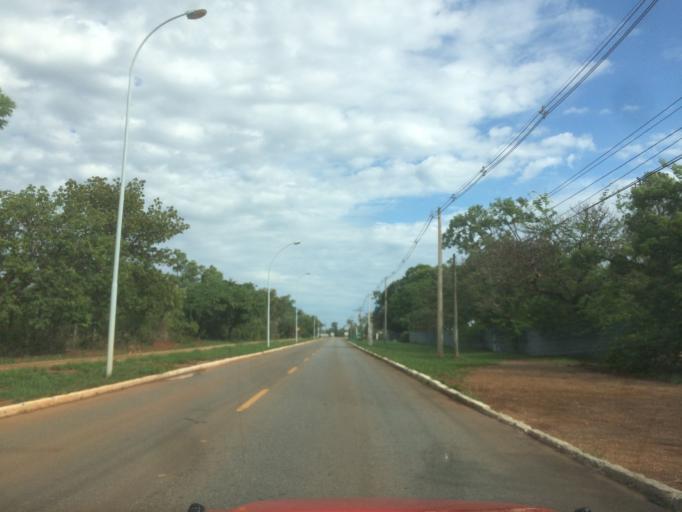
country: BR
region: Federal District
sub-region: Brasilia
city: Brasilia
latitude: -15.8103
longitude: -47.8370
